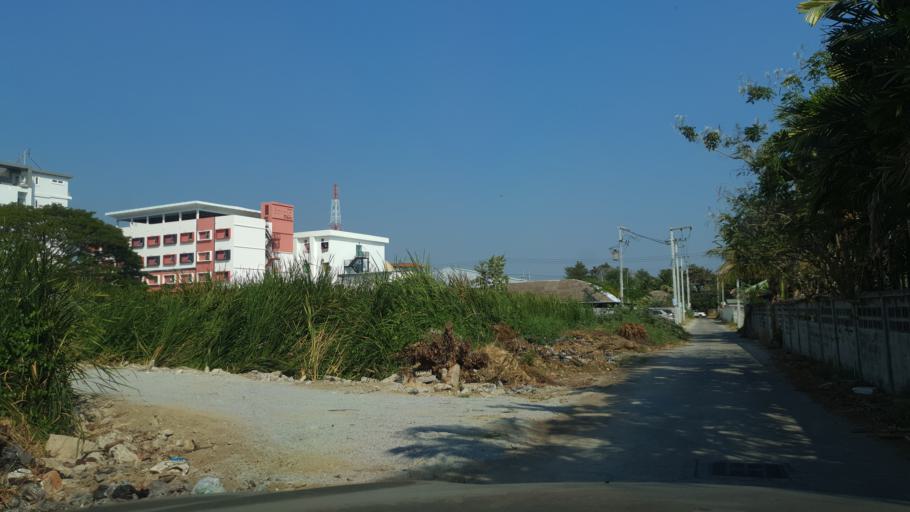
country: TH
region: Prachuap Khiri Khan
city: Hua Hin
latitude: 12.5529
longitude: 99.9551
